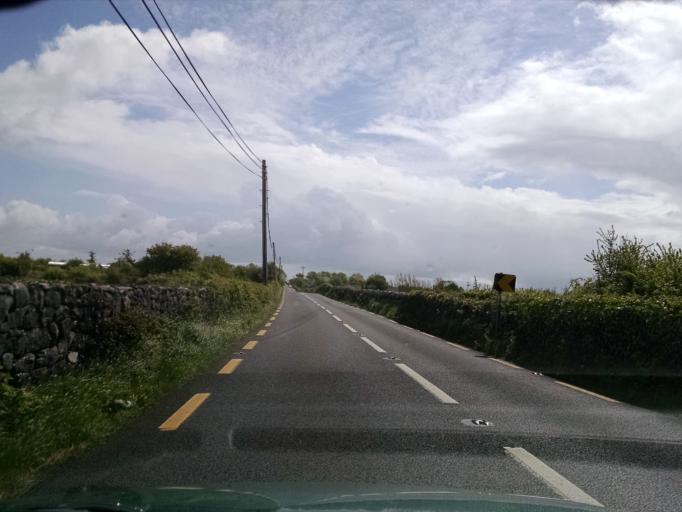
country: IE
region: Connaught
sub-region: County Galway
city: Oranmore
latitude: 53.1404
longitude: -8.9638
